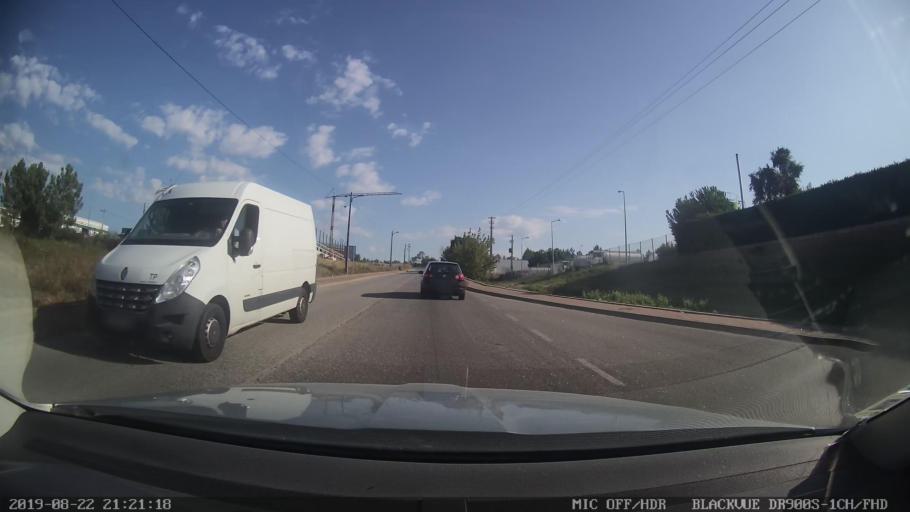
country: PT
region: Castelo Branco
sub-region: Serta
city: Serta
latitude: 39.8177
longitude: -8.1087
